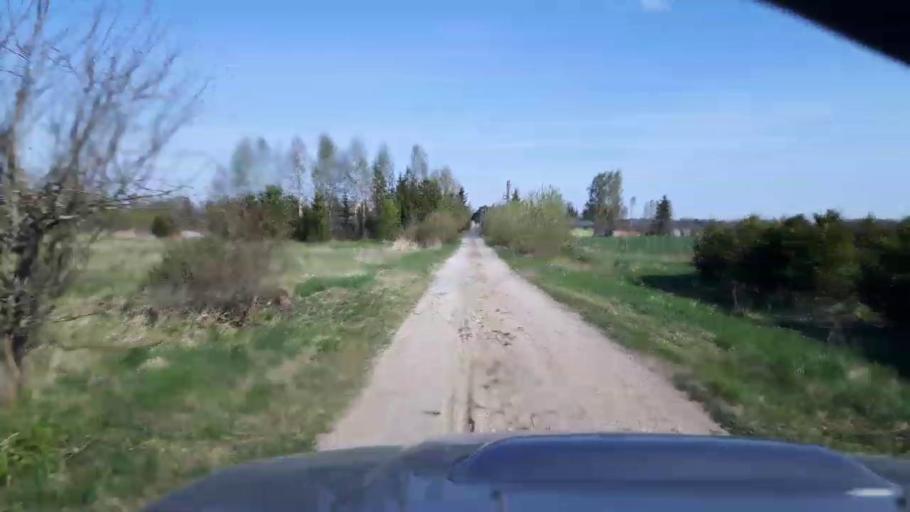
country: EE
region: Paernumaa
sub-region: Tootsi vald
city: Tootsi
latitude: 58.4920
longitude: 24.9075
